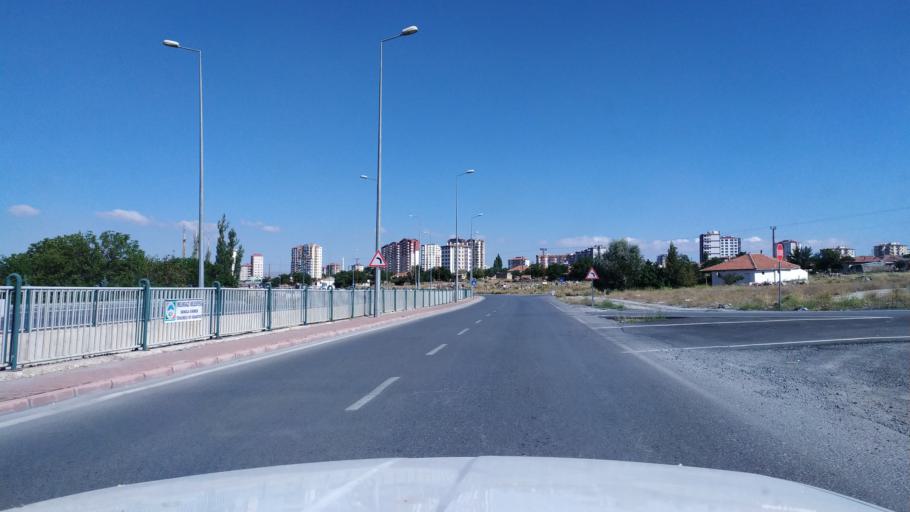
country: TR
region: Kayseri
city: Talas
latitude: 38.7316
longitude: 35.5492
